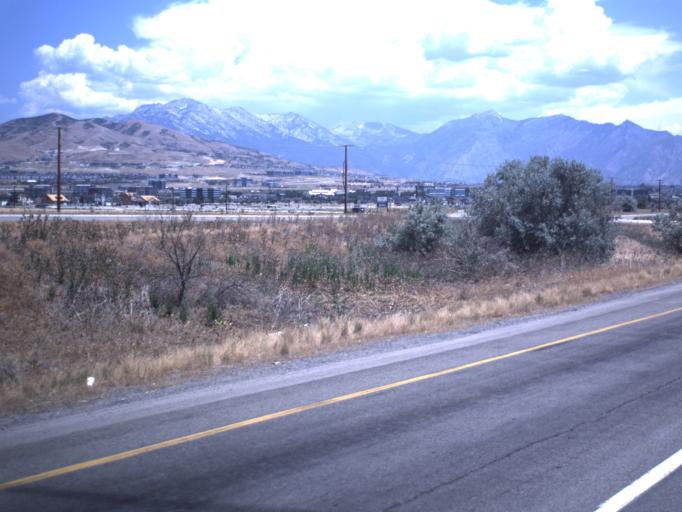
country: US
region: Utah
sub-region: Utah County
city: Lehi
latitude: 40.4125
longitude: -111.9084
